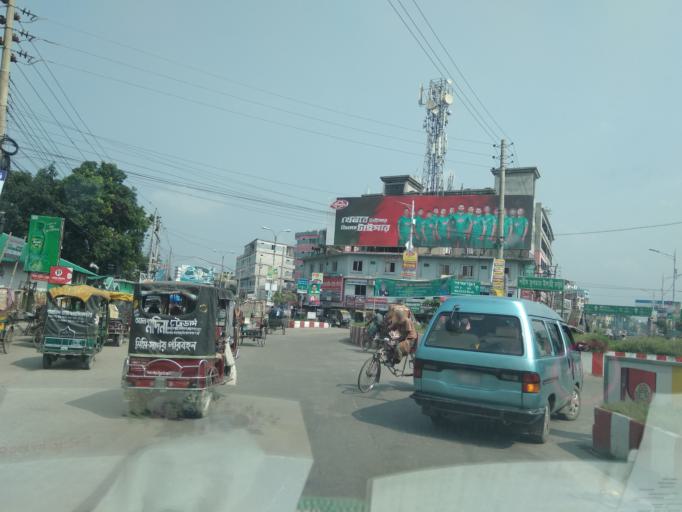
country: BD
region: Rangpur Division
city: Rangpur
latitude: 25.7654
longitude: 89.2313
